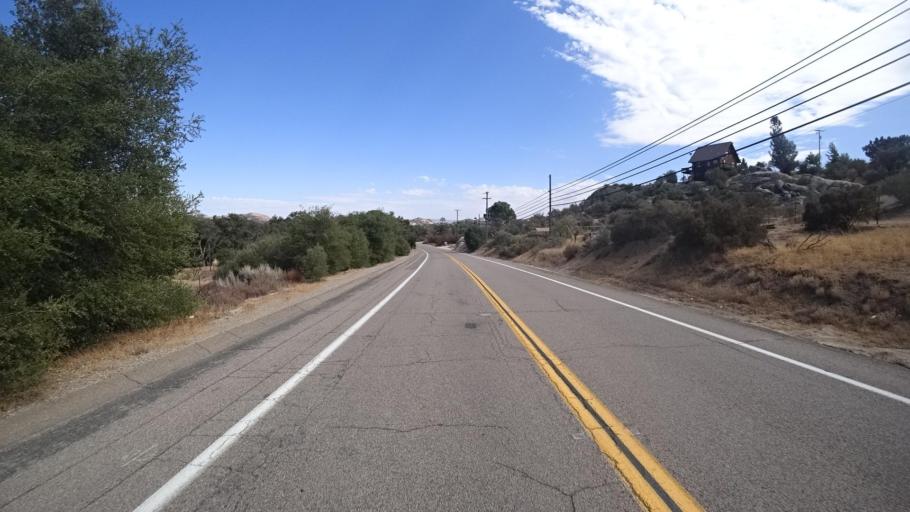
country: MX
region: Baja California
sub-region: Tecate
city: Cereso del Hongo
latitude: 32.6667
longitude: -116.2843
